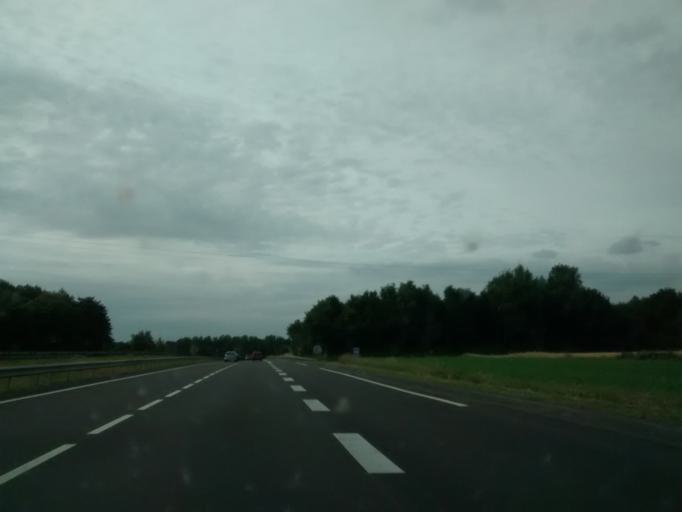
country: FR
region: Brittany
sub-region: Departement d'Ille-et-Vilaine
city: Quedillac
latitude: 48.2307
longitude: -2.1185
